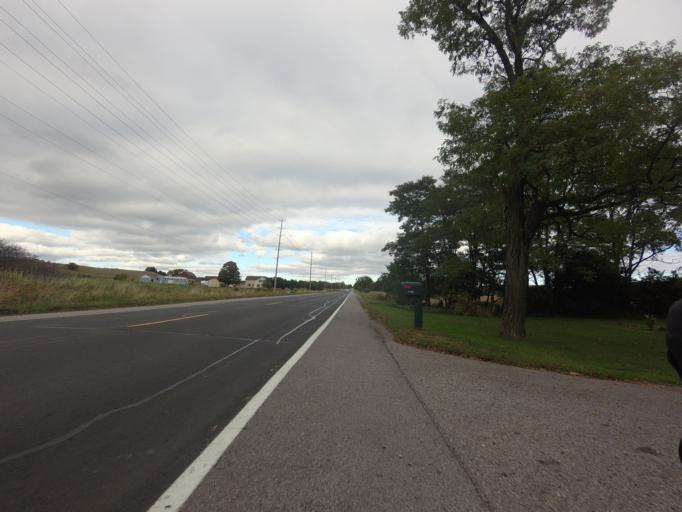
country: CA
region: Ontario
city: Cobourg
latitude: 43.9701
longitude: -78.1217
